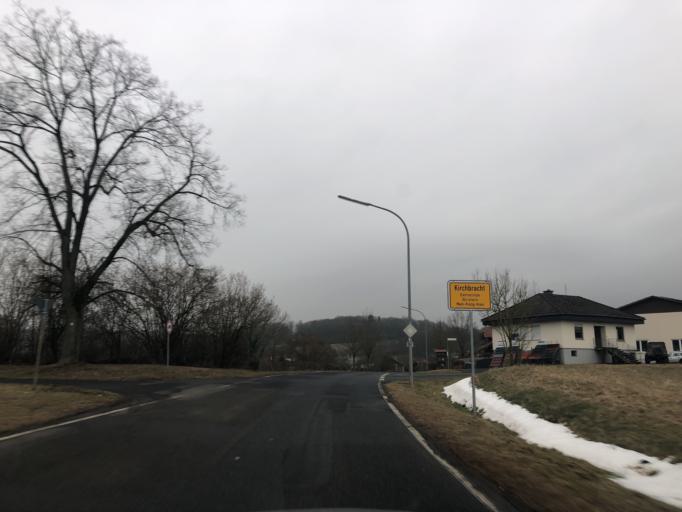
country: DE
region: Hesse
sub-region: Regierungsbezirk Darmstadt
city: Birstein
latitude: 50.4016
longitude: 9.2835
